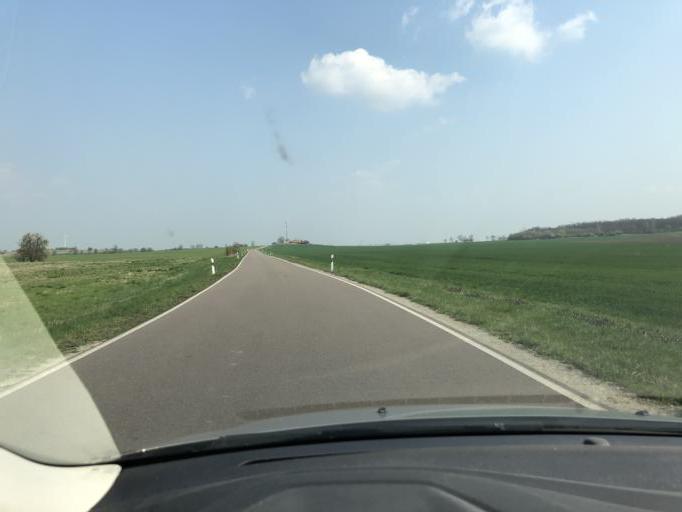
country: DE
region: Saxony-Anhalt
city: Oppin
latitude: 51.5631
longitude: 12.0613
